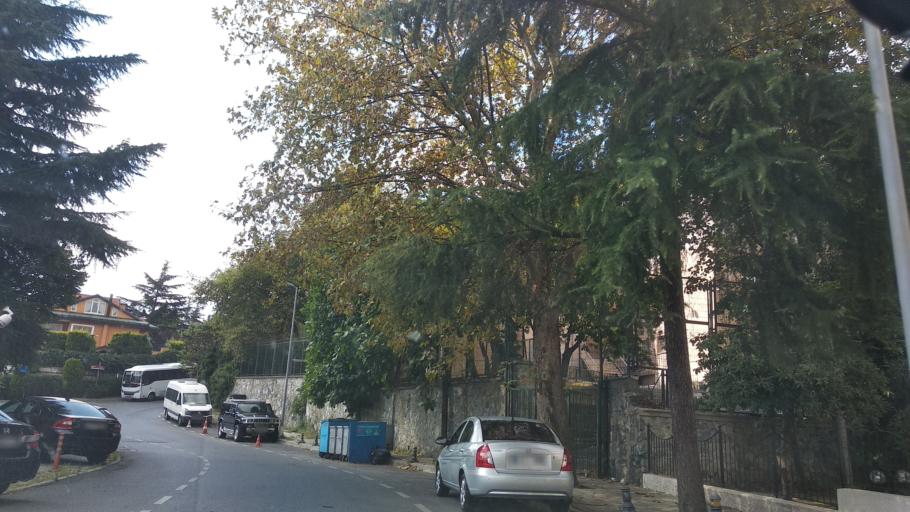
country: TR
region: Istanbul
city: Sisli
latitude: 41.0841
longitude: 29.0407
